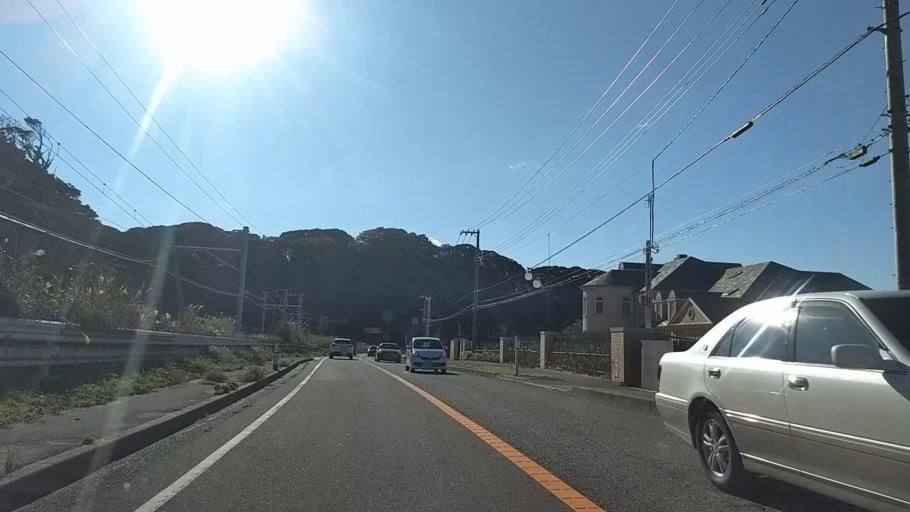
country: JP
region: Chiba
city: Futtsu
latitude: 35.1828
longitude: 139.8189
